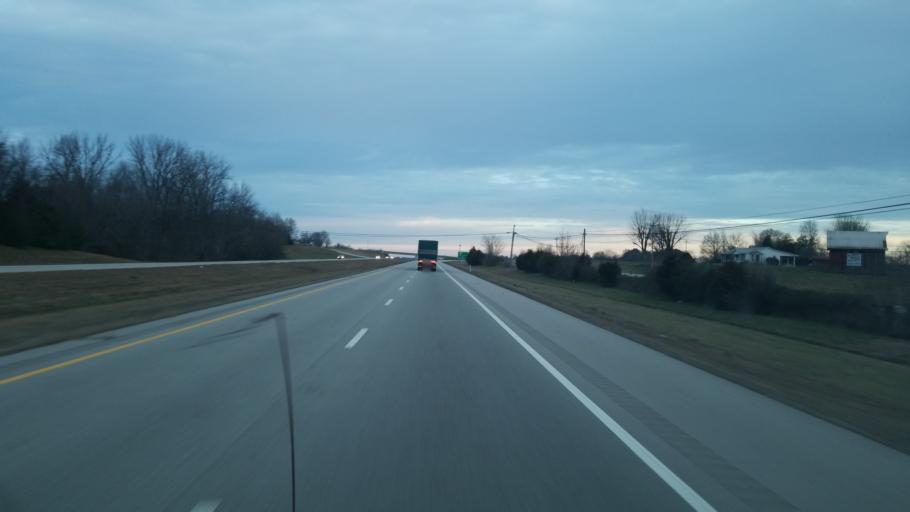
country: US
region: Tennessee
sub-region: Putnam County
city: Cookeville
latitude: 36.0478
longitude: -85.5078
